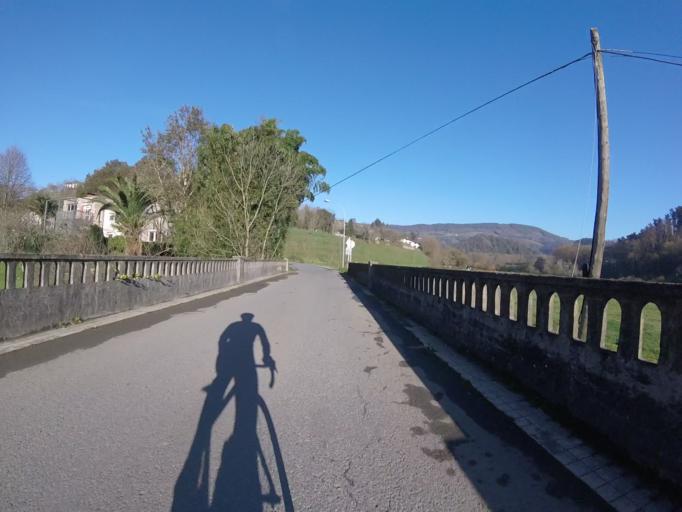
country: ES
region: Basque Country
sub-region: Provincia de Guipuzcoa
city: Usurbil
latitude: 43.2708
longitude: -2.0673
